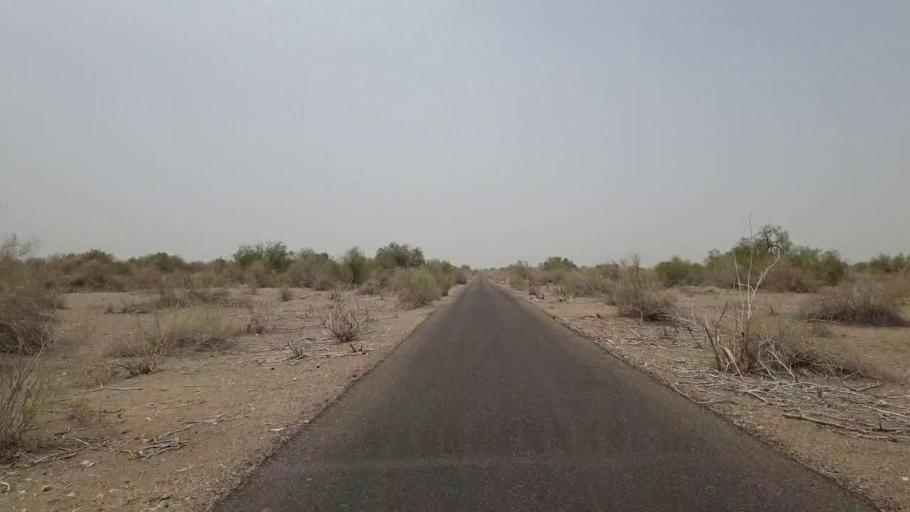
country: PK
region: Sindh
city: Islamkot
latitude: 24.7623
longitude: 70.4771
